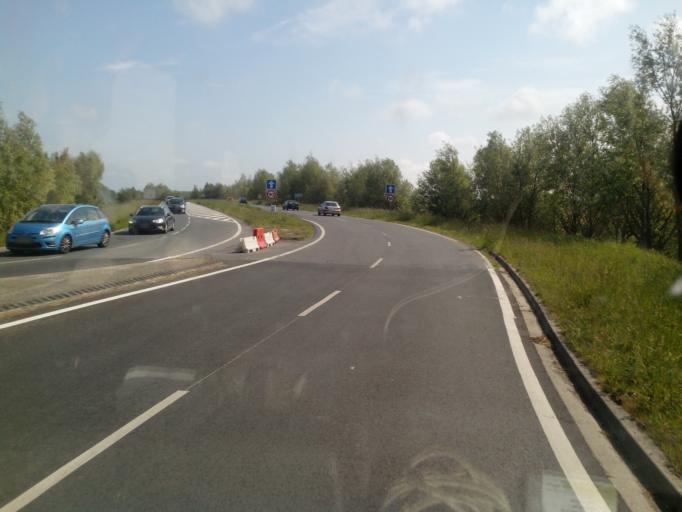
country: FR
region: Picardie
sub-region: Departement de la Somme
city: Quend
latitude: 50.3088
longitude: 1.6357
